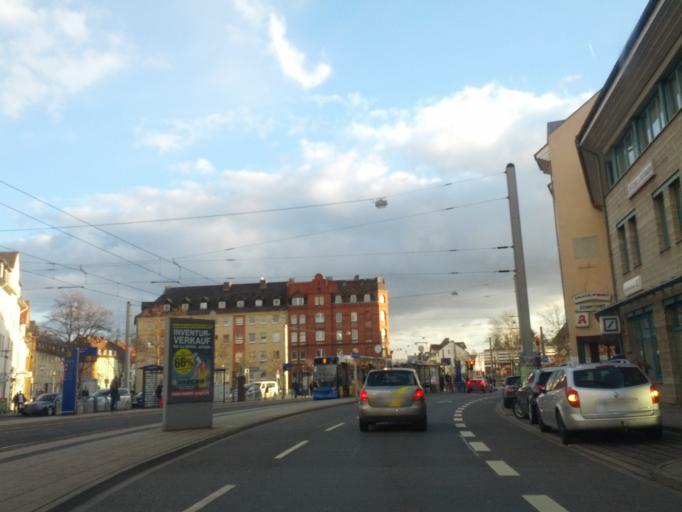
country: DE
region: Hesse
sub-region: Regierungsbezirk Kassel
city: Kassel
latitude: 51.3039
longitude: 9.5306
